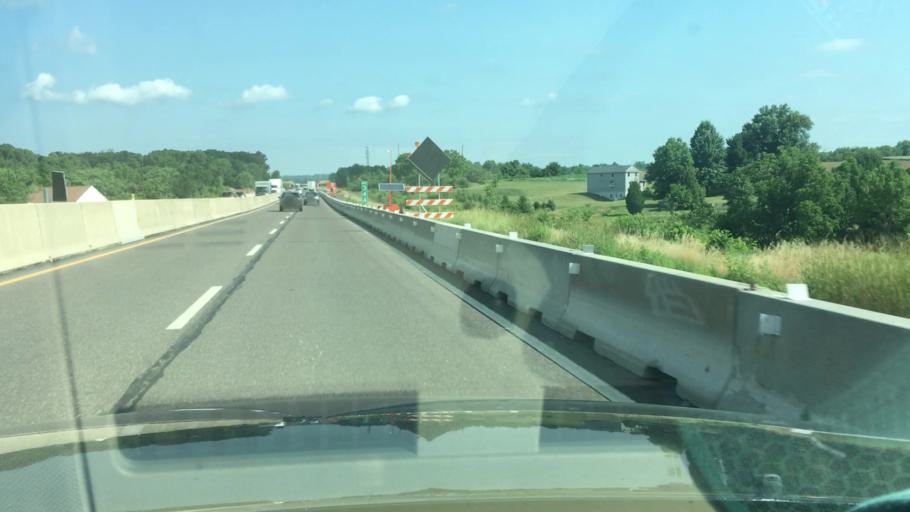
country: US
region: Pennsylvania
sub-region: Montgomery County
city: Harleysville
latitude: 40.3072
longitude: -75.3724
